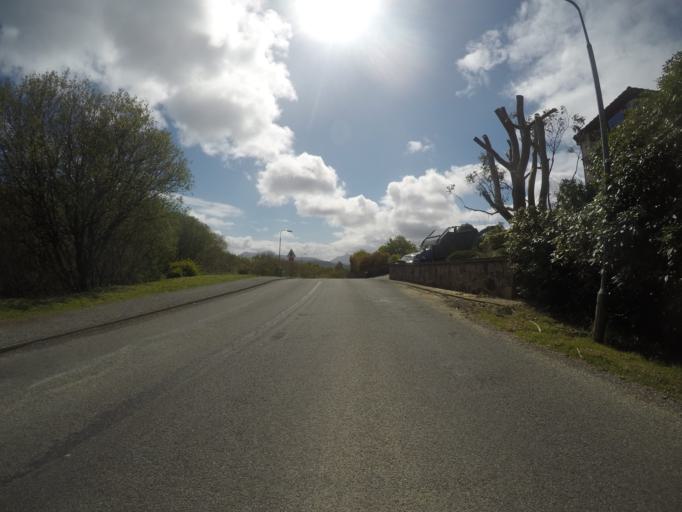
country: GB
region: Scotland
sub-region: Highland
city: Portree
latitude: 57.4230
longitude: -6.1893
